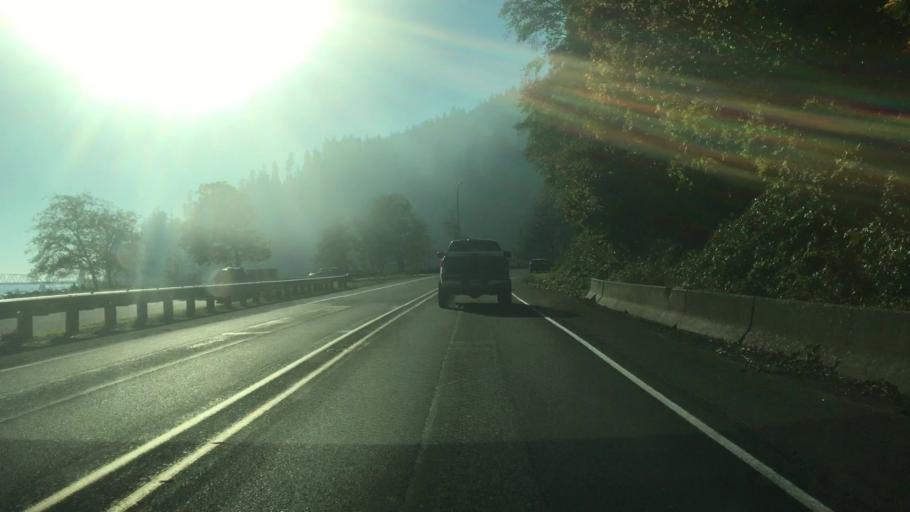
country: US
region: Oregon
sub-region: Clatsop County
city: Astoria
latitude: 46.2494
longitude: -123.8608
